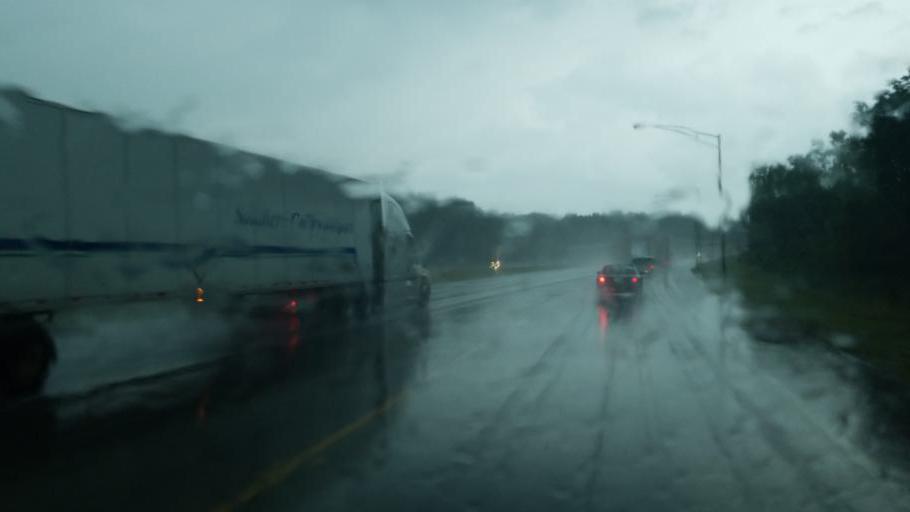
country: US
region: Ohio
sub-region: Trumbull County
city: Churchill
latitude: 41.1569
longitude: -80.6616
